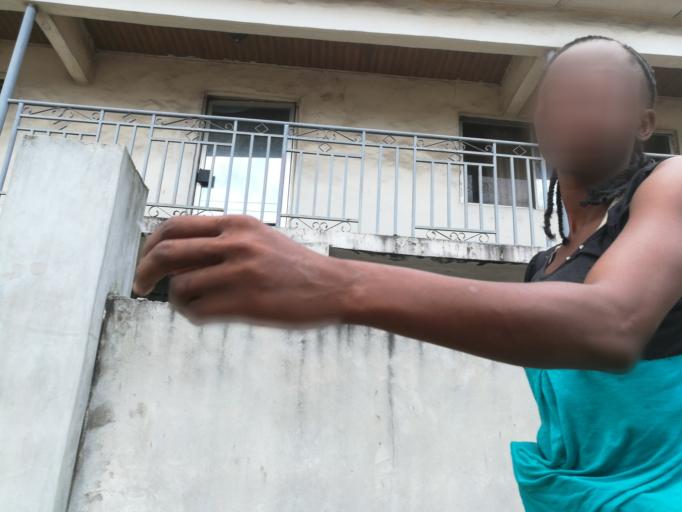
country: NG
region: Rivers
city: Okrika
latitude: 4.7260
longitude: 7.1512
